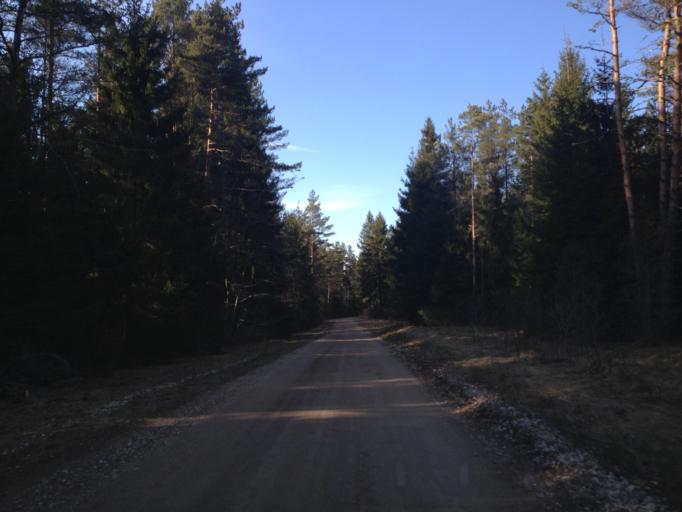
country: EE
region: Harju
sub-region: Nissi vald
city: Turba
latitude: 59.1090
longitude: 24.1574
